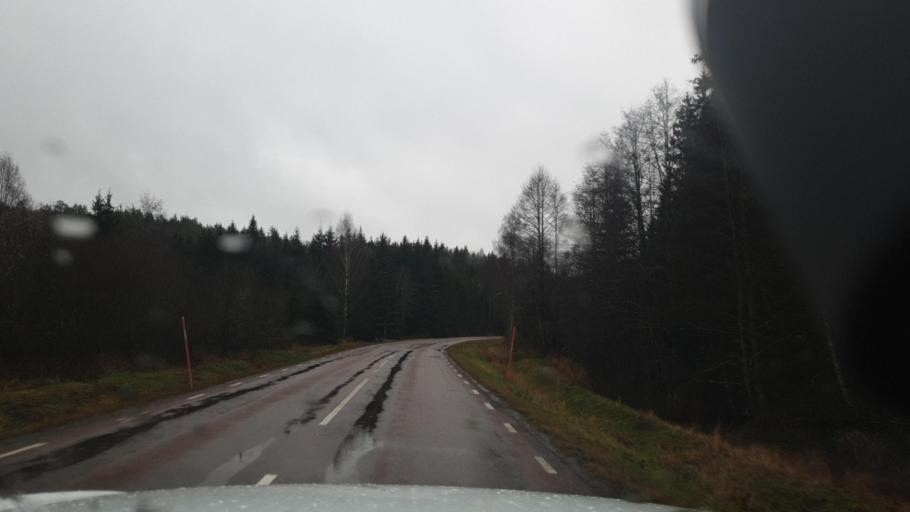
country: SE
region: Vaermland
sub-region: Grums Kommun
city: Slottsbron
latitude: 59.4244
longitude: 12.9800
